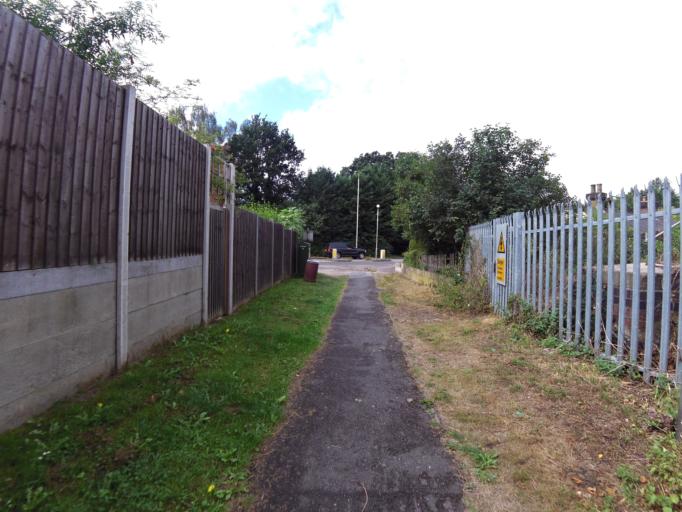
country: GB
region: England
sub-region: Hertfordshire
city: Radlett
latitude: 51.6931
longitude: -0.3220
